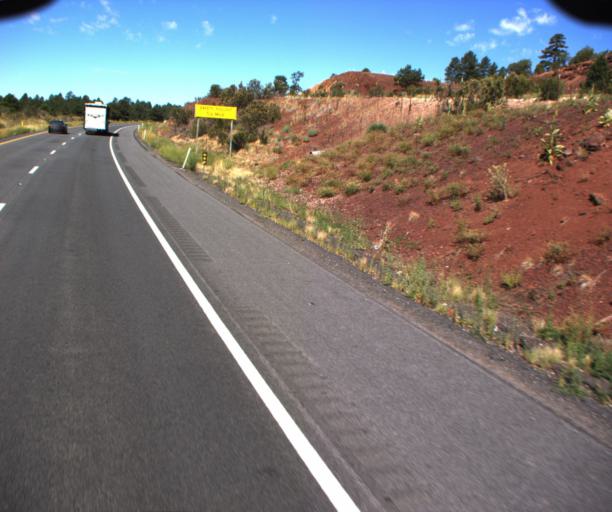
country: US
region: Arizona
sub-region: Coconino County
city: Williams
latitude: 35.2202
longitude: -112.3026
